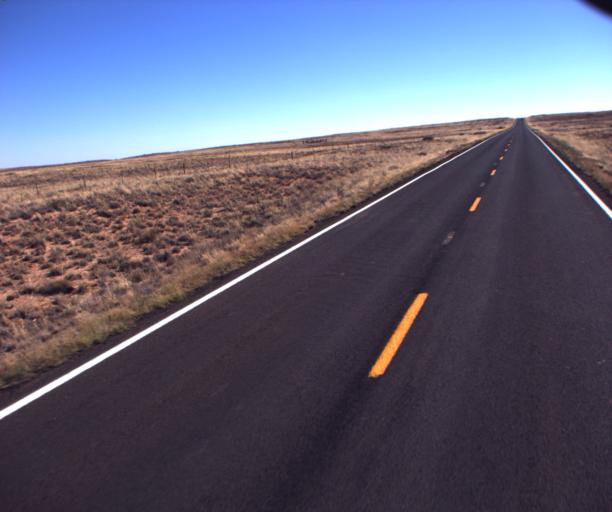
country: US
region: Arizona
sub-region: Coconino County
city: Tuba City
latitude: 35.9763
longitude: -110.9772
